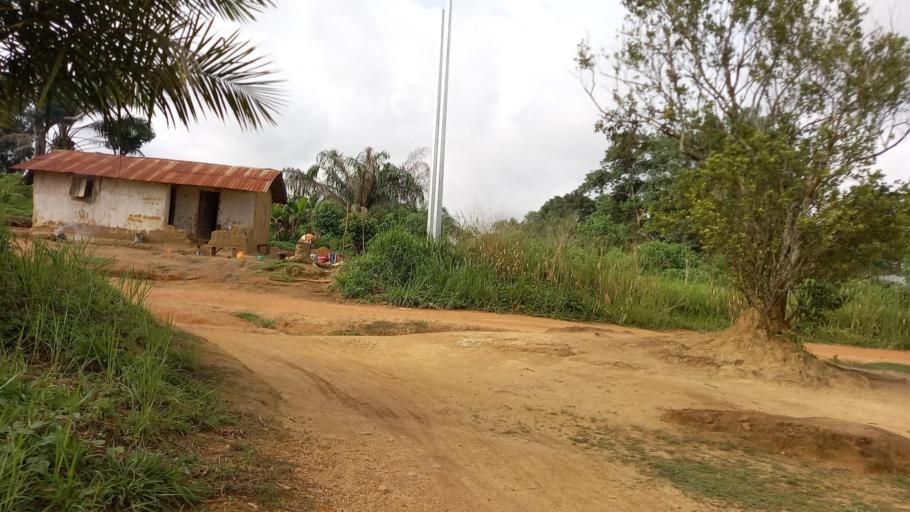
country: SL
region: Eastern Province
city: Kailahun
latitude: 8.2830
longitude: -10.5776
